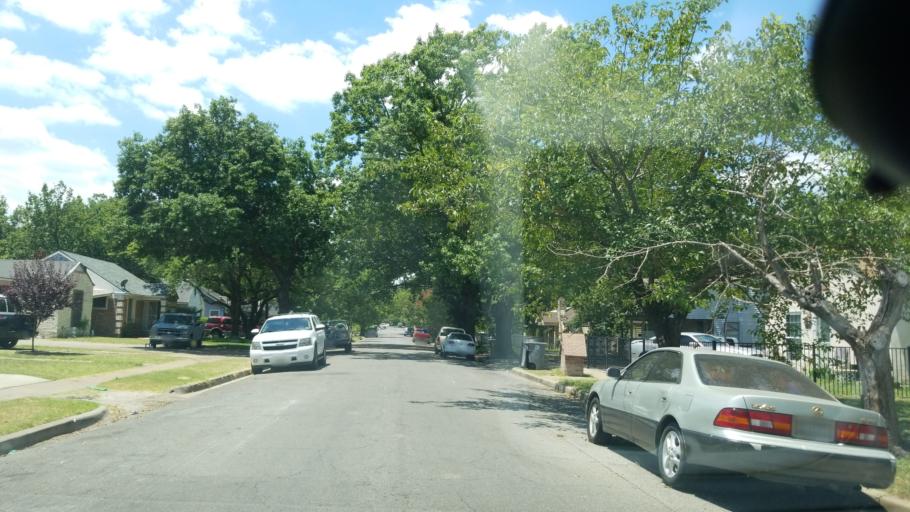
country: US
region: Texas
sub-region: Dallas County
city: Cockrell Hill
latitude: 32.7223
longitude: -96.8427
